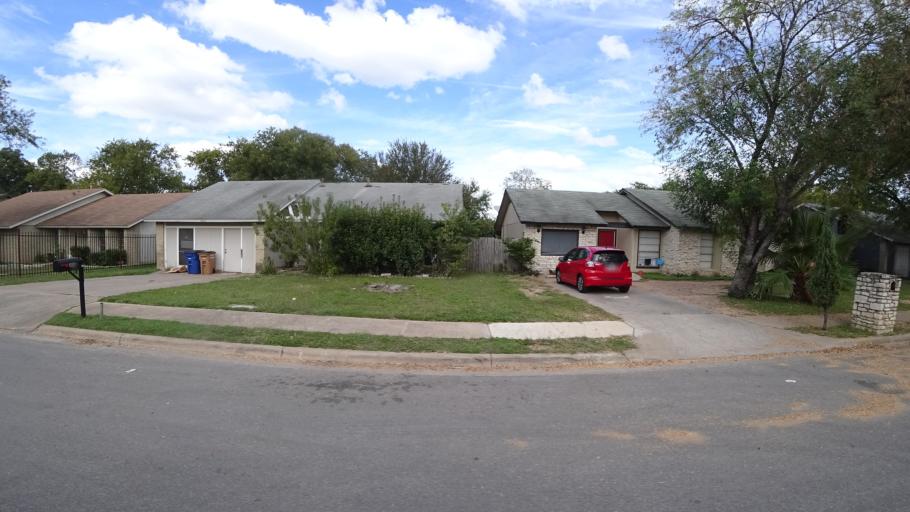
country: US
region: Texas
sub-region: Travis County
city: Austin
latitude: 30.2011
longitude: -97.7406
